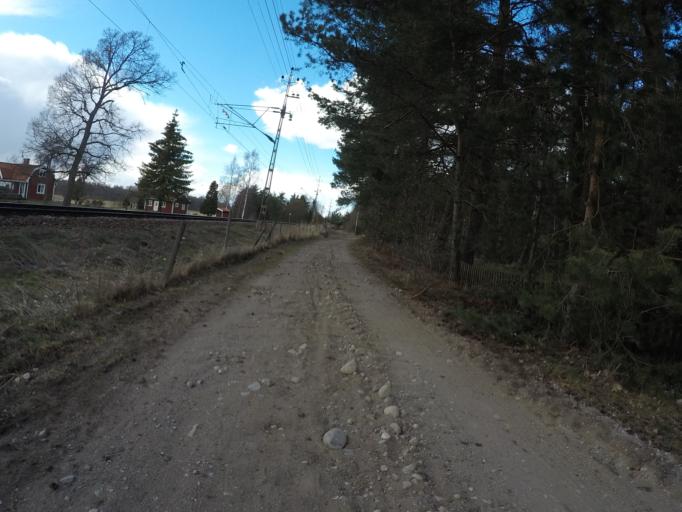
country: SE
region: Soedermanland
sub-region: Eskilstuna Kommun
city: Kvicksund
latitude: 59.4966
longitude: 16.2733
